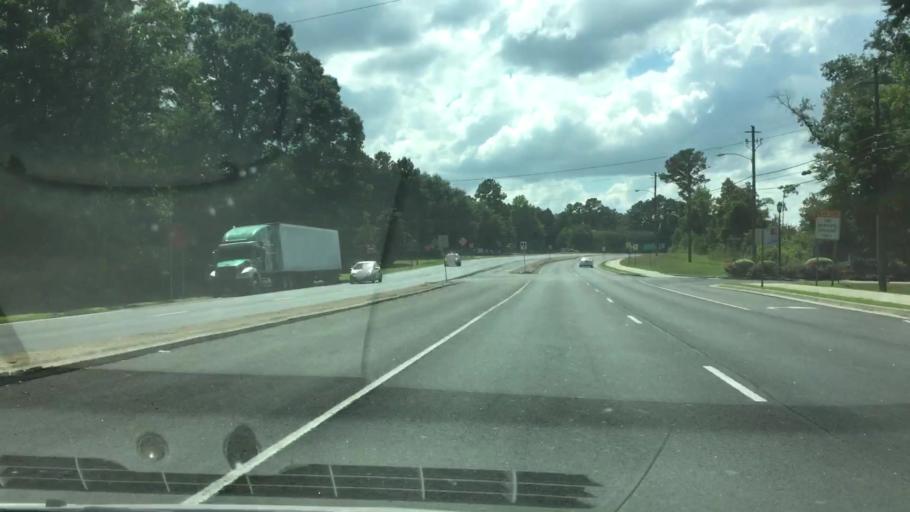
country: US
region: Georgia
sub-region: Fayette County
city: Fayetteville
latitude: 33.4520
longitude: -84.4318
